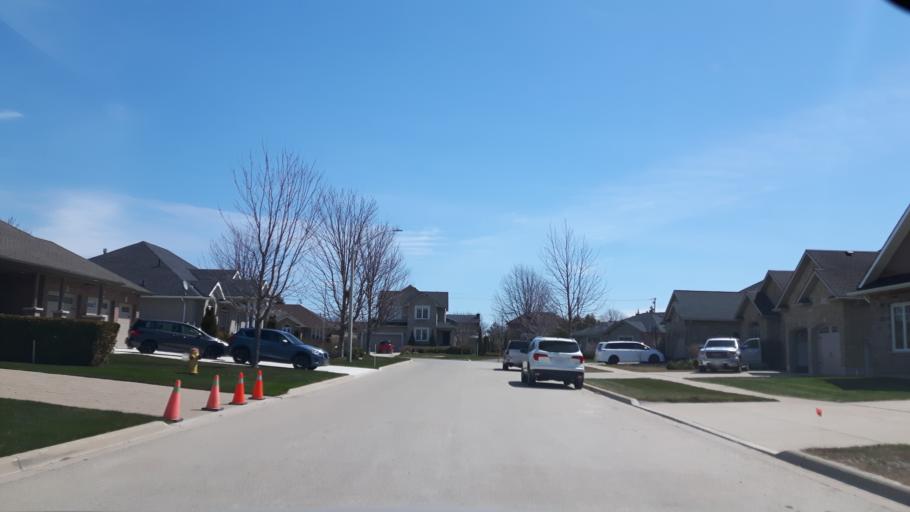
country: CA
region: Ontario
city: Goderich
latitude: 43.7285
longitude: -81.7183
